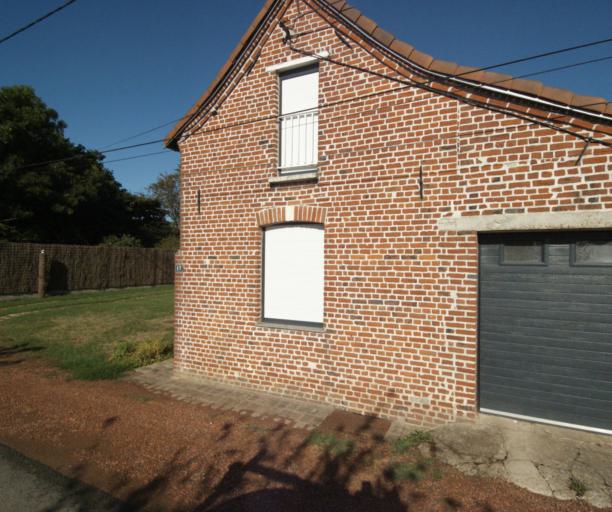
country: FR
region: Nord-Pas-de-Calais
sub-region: Departement du Nord
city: Willems
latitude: 50.6452
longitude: 3.2437
